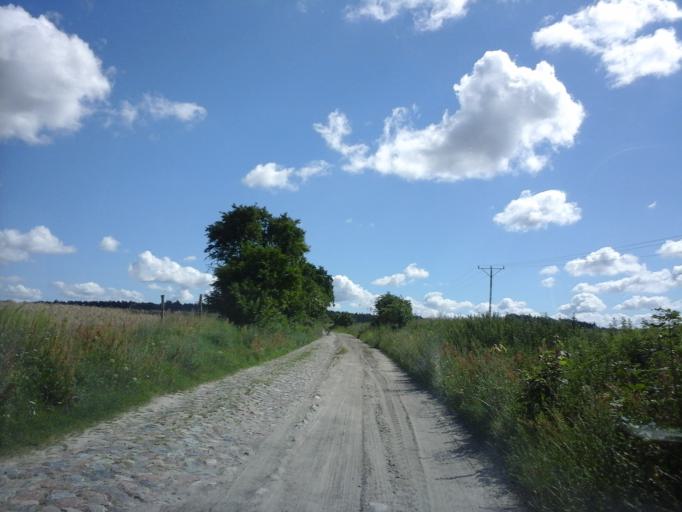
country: PL
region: West Pomeranian Voivodeship
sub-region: Powiat choszczenski
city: Recz
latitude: 53.2124
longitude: 15.5107
